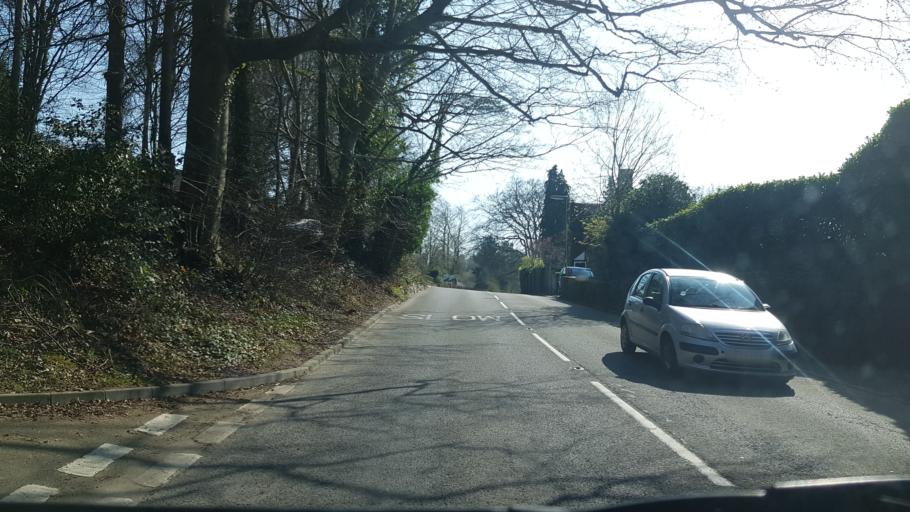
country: GB
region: England
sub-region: Surrey
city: Haslemere
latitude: 51.0847
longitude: -0.7336
